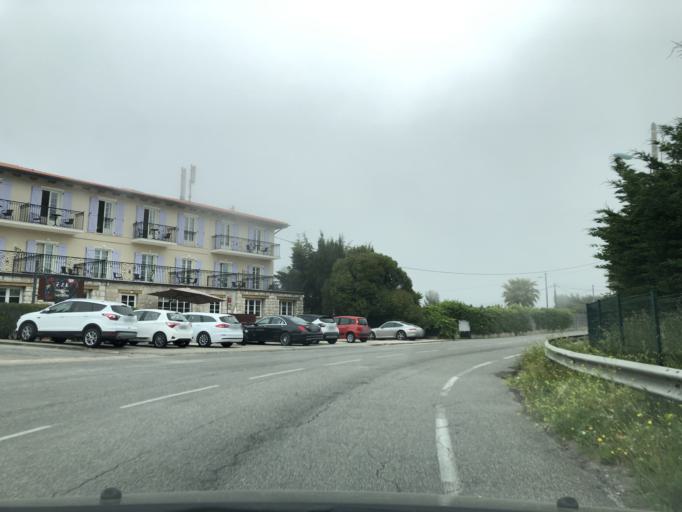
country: FR
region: Provence-Alpes-Cote d'Azur
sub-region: Departement des Alpes-Maritimes
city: Beaulieu-sur-Mer
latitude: 43.7310
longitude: 7.3417
